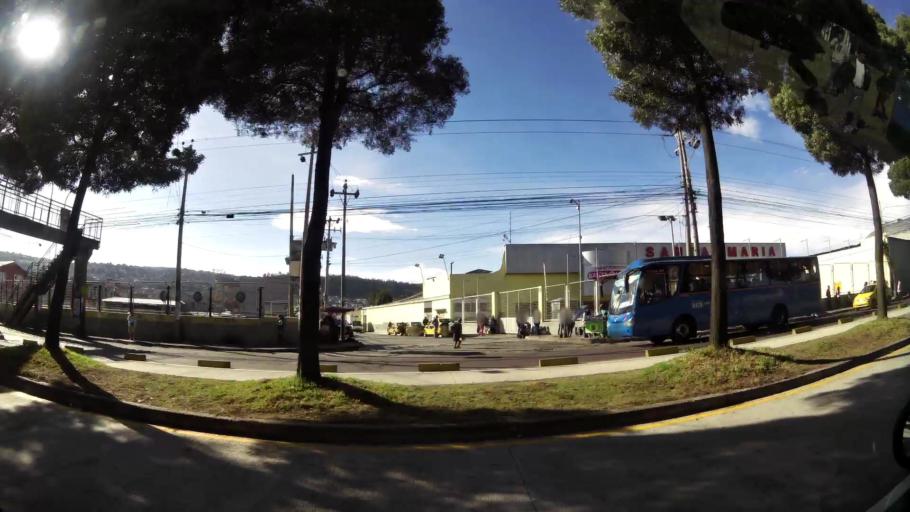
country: EC
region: Pichincha
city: Quito
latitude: -0.3077
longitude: -78.5444
